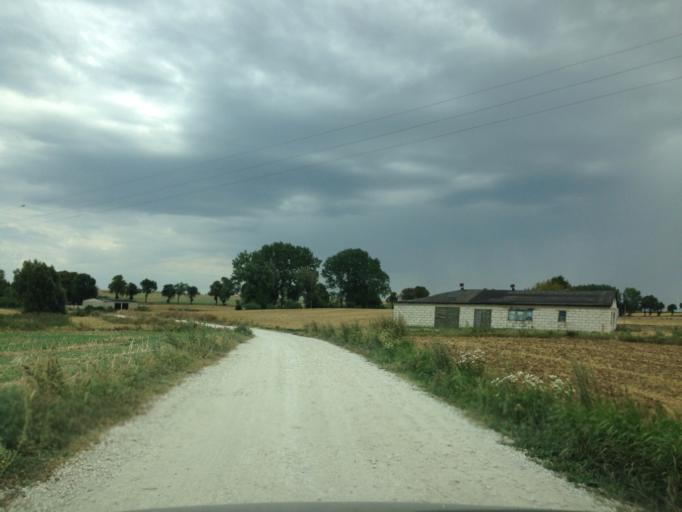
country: PL
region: Kujawsko-Pomorskie
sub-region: Powiat golubsko-dobrzynski
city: Kowalewo Pomorskie
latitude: 53.1777
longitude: 18.8387
